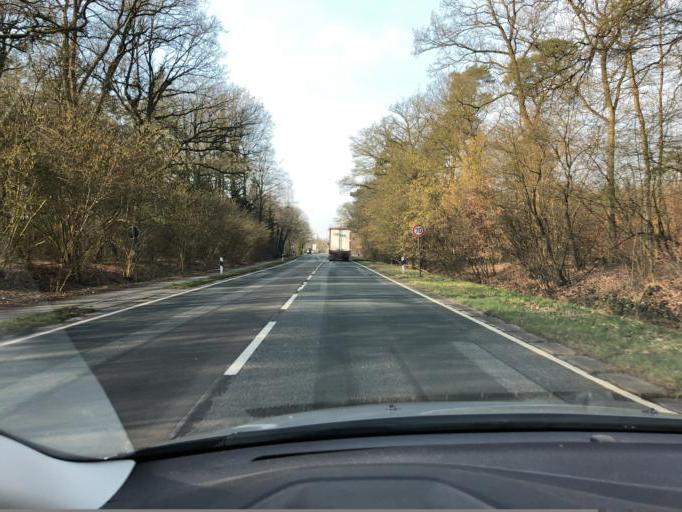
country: DE
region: Lower Saxony
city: Hesel
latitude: 53.3058
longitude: 7.6055
